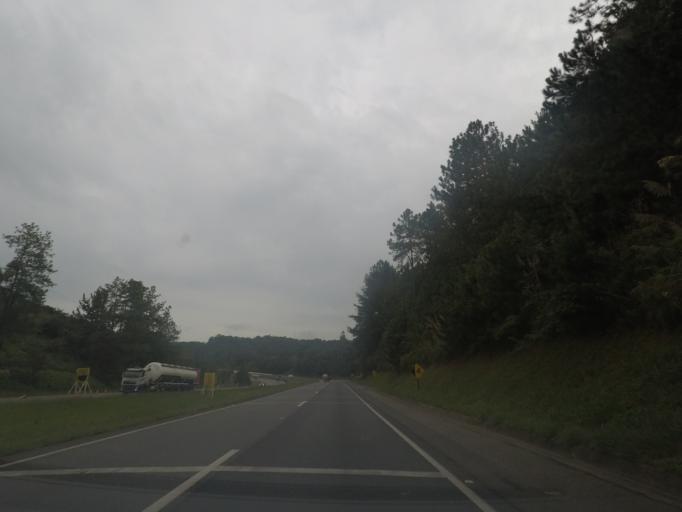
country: BR
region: Parana
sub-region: Campina Grande Do Sul
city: Campina Grande do Sul
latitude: -25.1999
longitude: -48.8953
